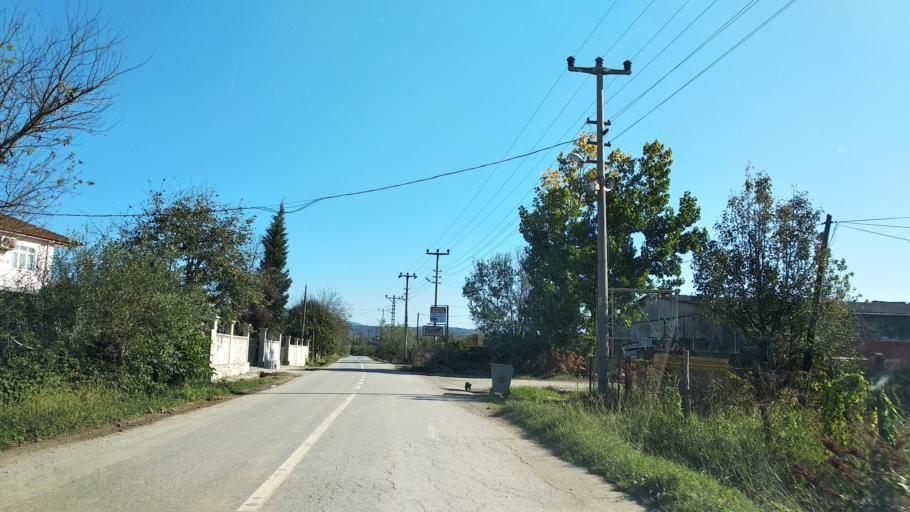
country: TR
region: Sakarya
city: Ortakoy
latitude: 41.0272
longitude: 30.5962
